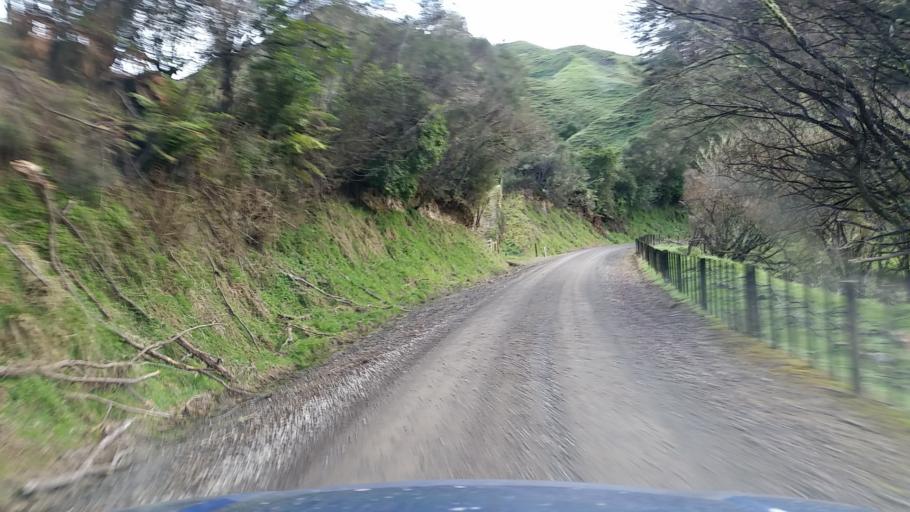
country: NZ
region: Taranaki
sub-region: New Plymouth District
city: Waitara
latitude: -39.0991
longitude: 174.8377
